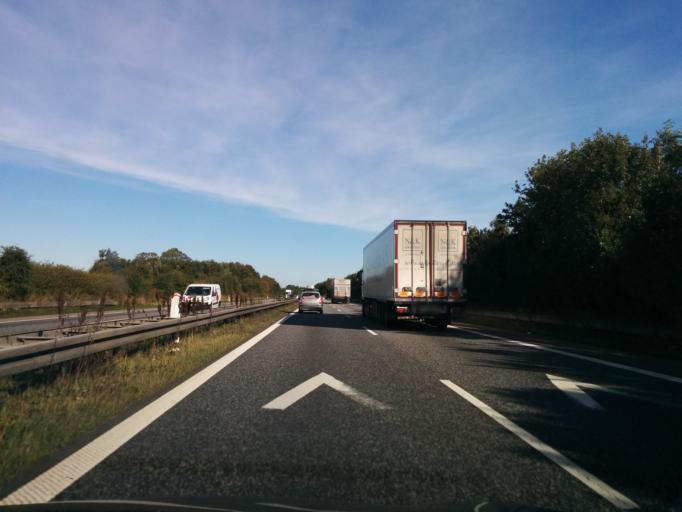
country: DK
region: Central Jutland
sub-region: Horsens Kommune
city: Horsens
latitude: 55.8650
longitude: 9.7633
